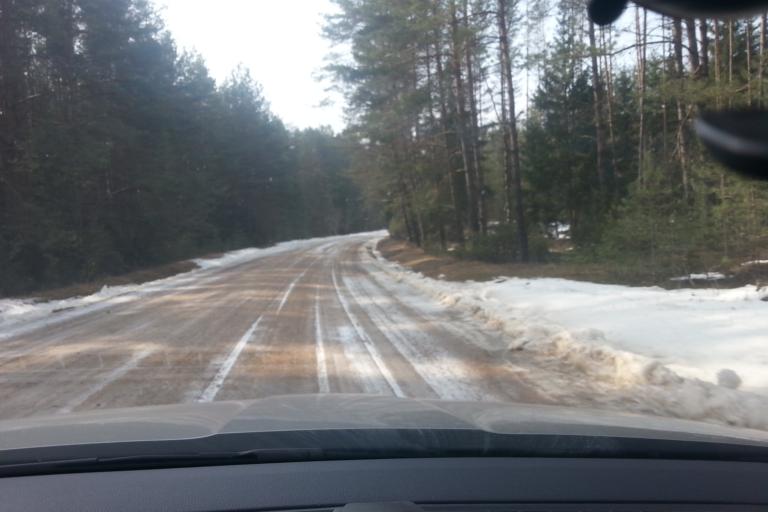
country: LT
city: Trakai
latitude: 54.5246
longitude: 24.9635
